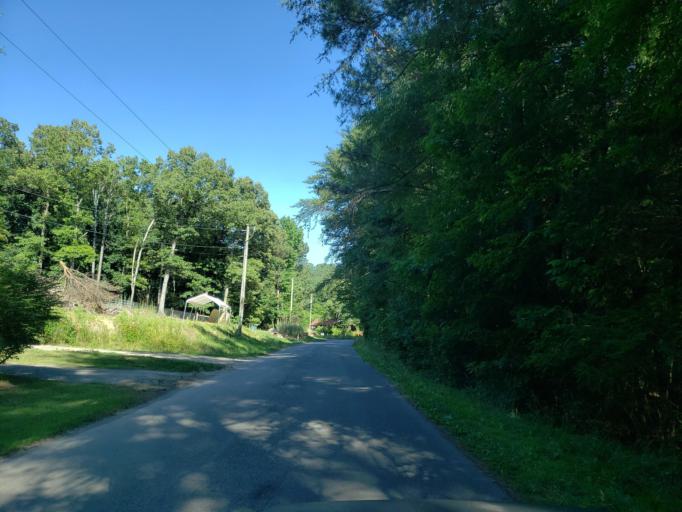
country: US
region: Georgia
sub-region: Whitfield County
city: Dalton
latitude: 34.6628
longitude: -85.0957
